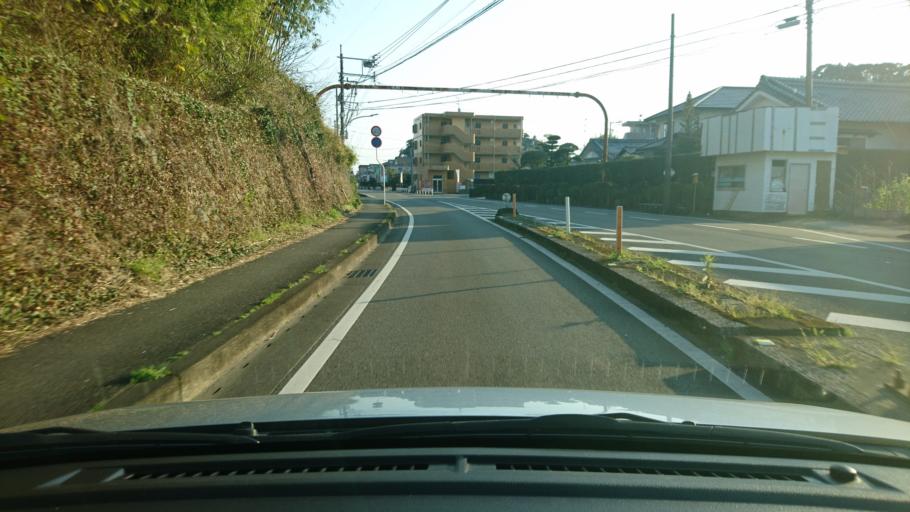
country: JP
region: Miyazaki
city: Miyazaki-shi
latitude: 31.9719
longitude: 131.4397
